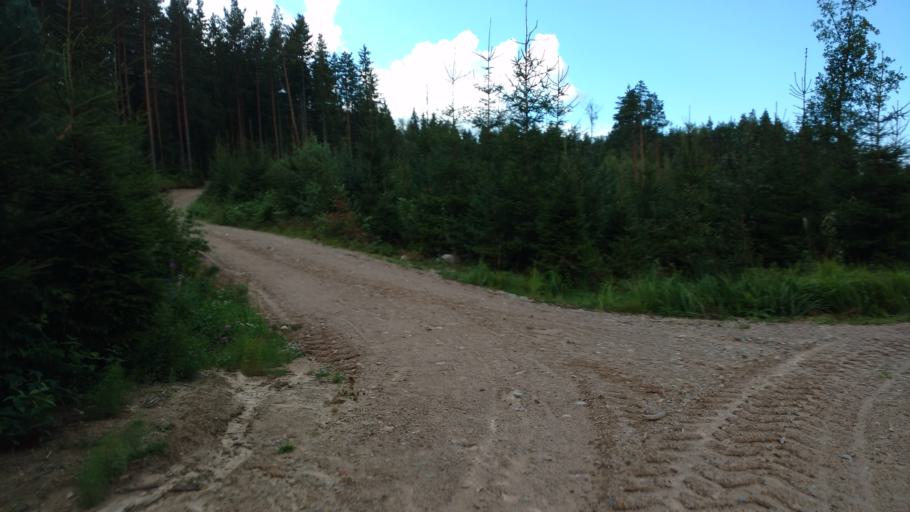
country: FI
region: Varsinais-Suomi
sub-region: Salo
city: Salo
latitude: 60.3556
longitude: 23.1570
